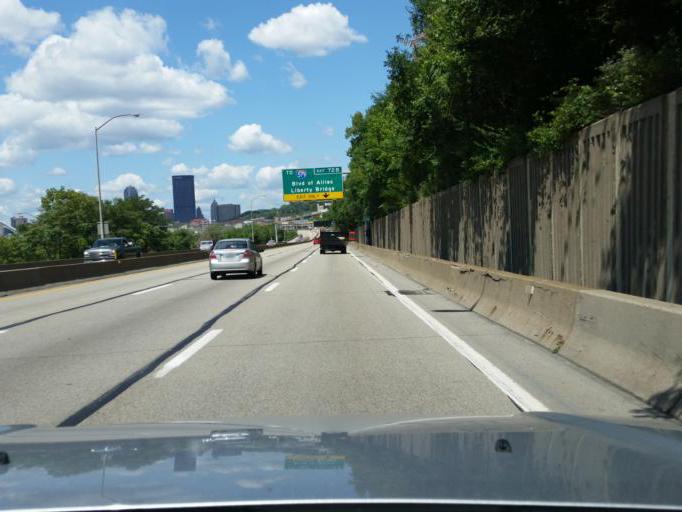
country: US
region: Pennsylvania
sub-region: Allegheny County
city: Bloomfield
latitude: 40.4328
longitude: -79.9613
